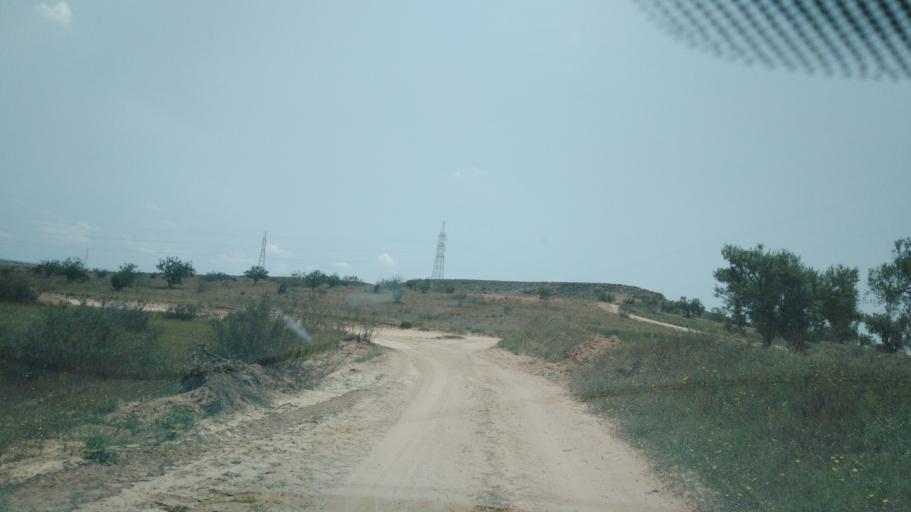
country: TN
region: Safaqis
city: Sfax
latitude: 34.7655
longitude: 10.5818
